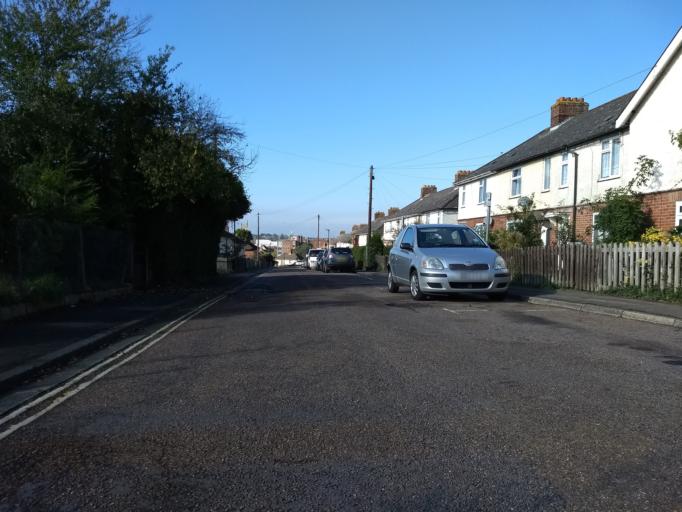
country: GB
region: England
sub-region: Isle of Wight
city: Newport
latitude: 50.7011
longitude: -1.2852
